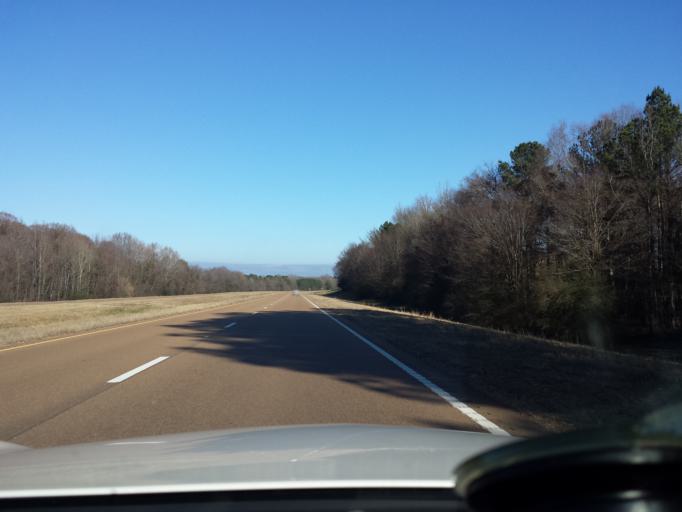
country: US
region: Mississippi
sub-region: Leake County
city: Carthage
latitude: 32.6532
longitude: -89.6515
